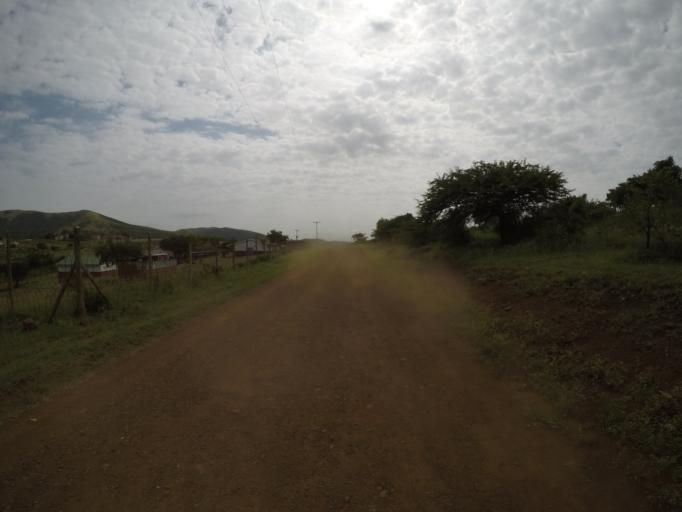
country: ZA
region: KwaZulu-Natal
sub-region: uThungulu District Municipality
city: Empangeni
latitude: -28.6217
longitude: 31.9035
